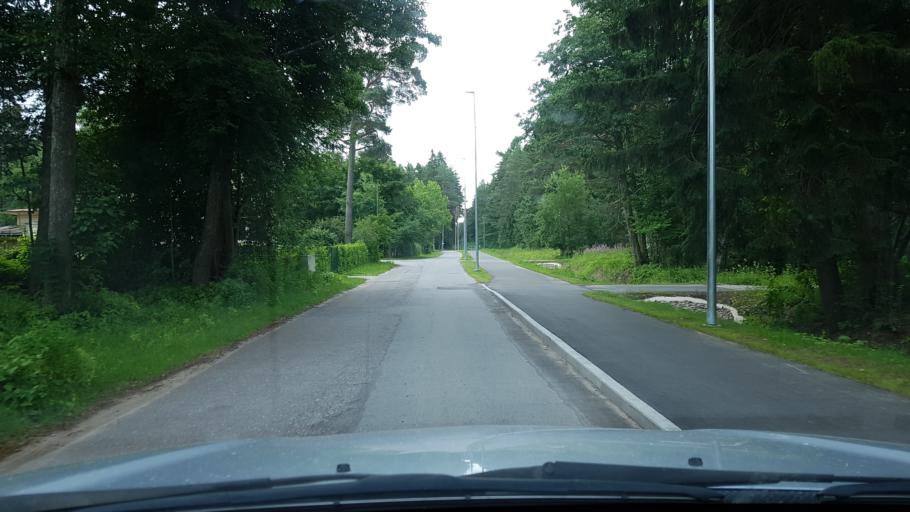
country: EE
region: Ida-Virumaa
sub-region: Narva-Joesuu linn
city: Narva-Joesuu
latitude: 59.4460
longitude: 28.0208
